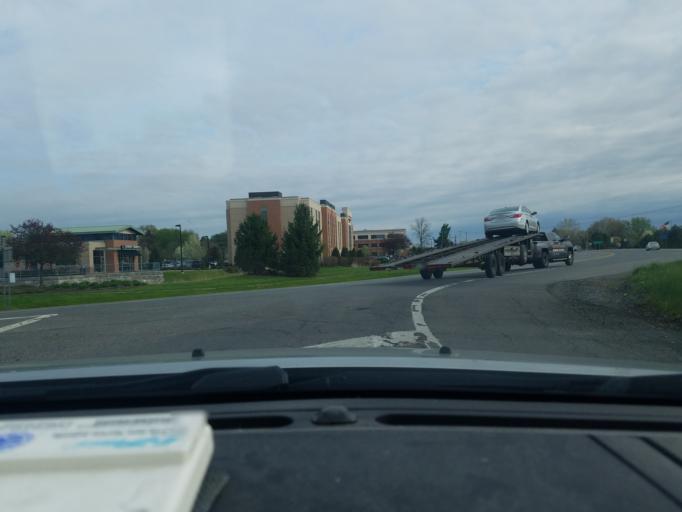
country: US
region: New York
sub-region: Onondaga County
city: East Syracuse
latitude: 43.0877
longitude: -76.0789
